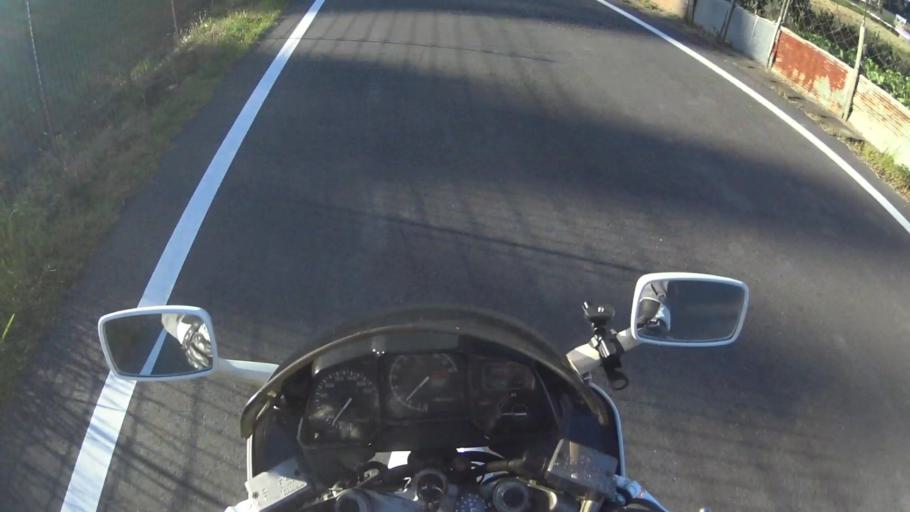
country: JP
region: Hyogo
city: Toyooka
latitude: 35.6088
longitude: 134.8881
